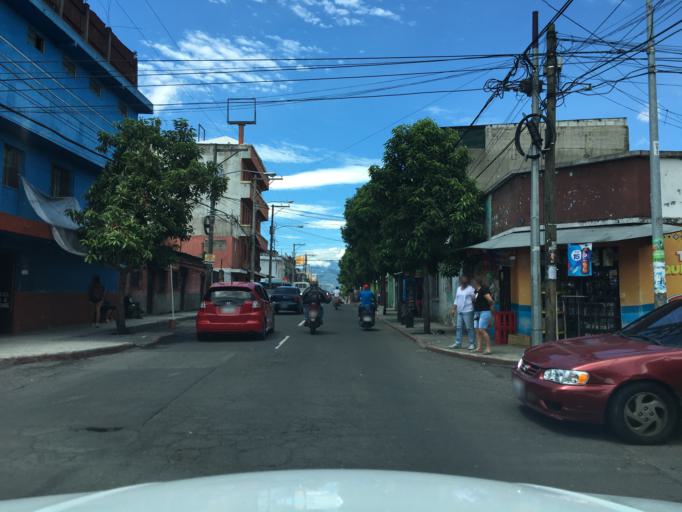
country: GT
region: Guatemala
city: Guatemala City
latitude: 14.6216
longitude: -90.5422
